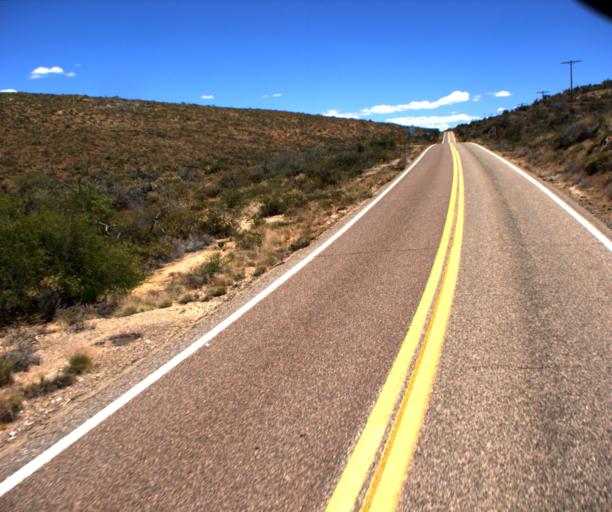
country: US
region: Arizona
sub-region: Yavapai County
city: Bagdad
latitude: 34.4438
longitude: -112.9530
